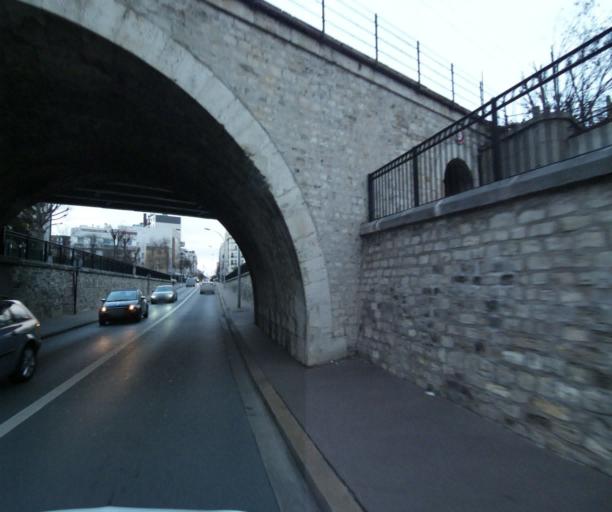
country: FR
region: Ile-de-France
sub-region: Departement des Hauts-de-Seine
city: Courbevoie
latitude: 48.9011
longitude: 2.2563
